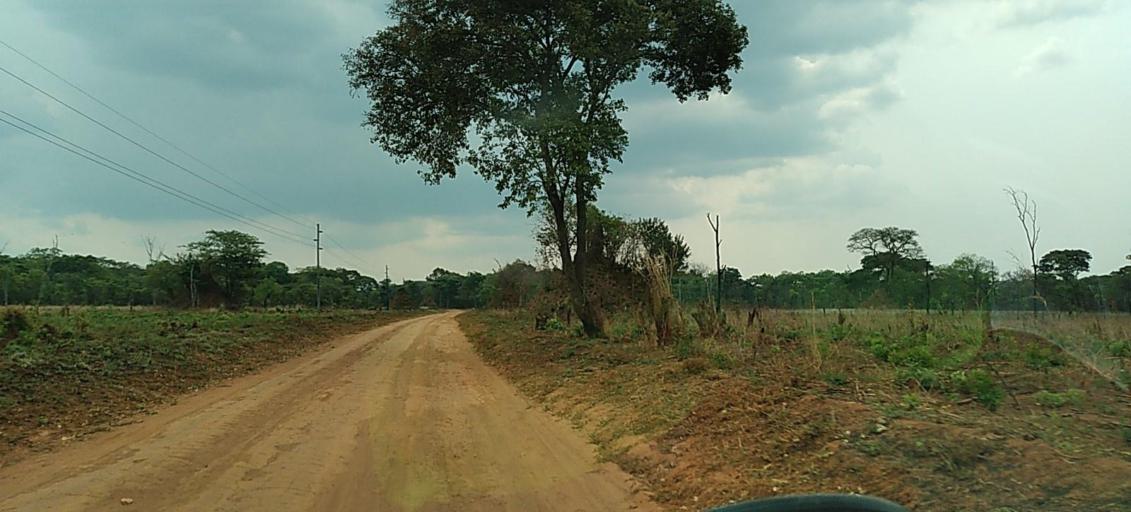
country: ZM
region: North-Western
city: Solwezi
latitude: -12.7818
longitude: 26.4950
